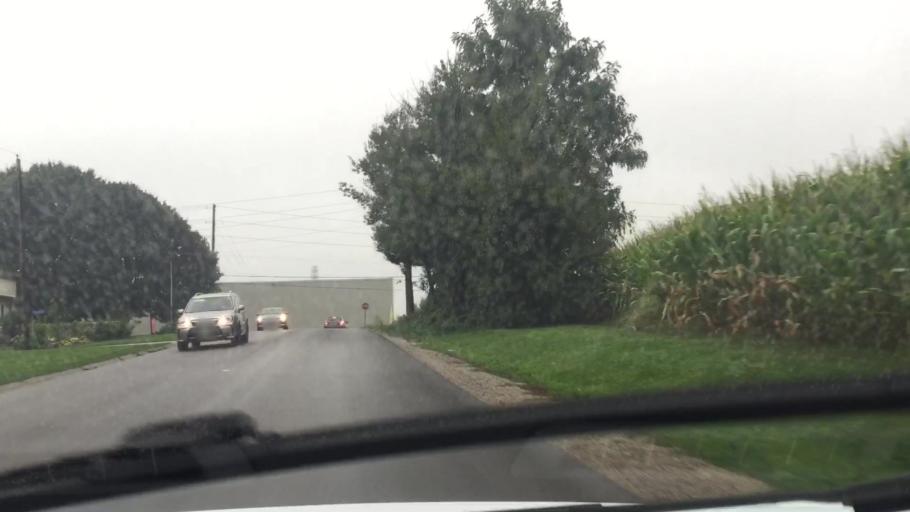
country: CA
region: Ontario
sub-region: Oxford County
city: Woodstock
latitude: 43.1078
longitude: -80.7314
